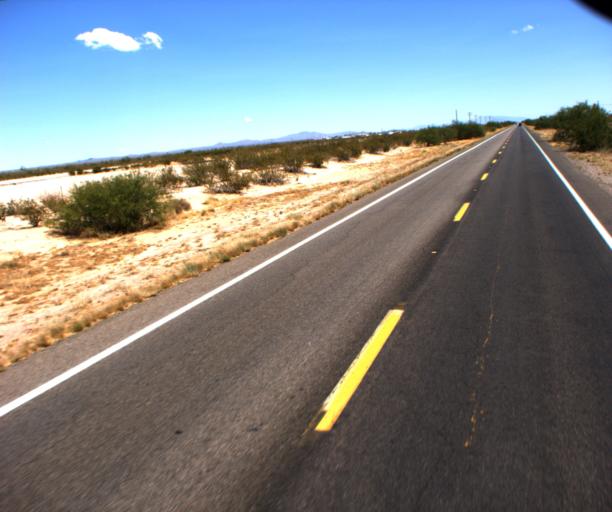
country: US
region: Arizona
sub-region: Pinal County
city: Florence
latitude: 32.9848
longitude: -111.3587
